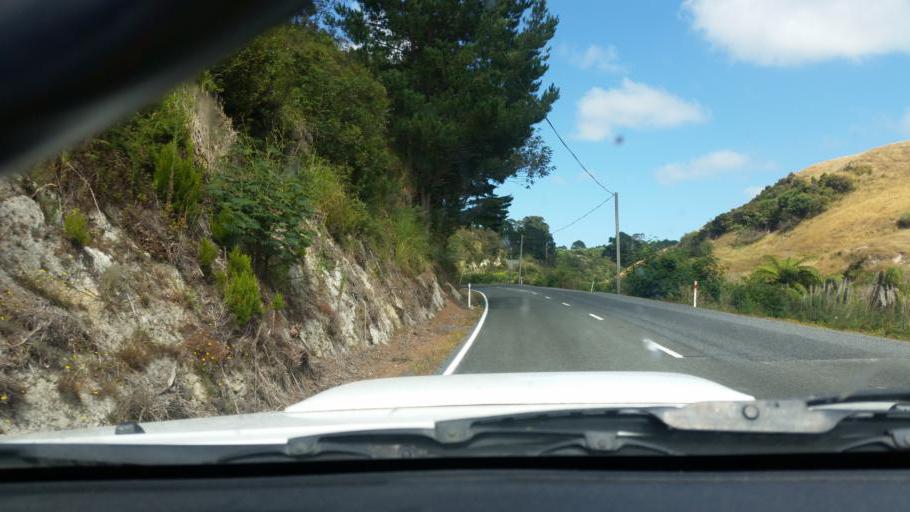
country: NZ
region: Northland
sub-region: Kaipara District
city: Dargaville
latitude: -35.8225
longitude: 173.6979
